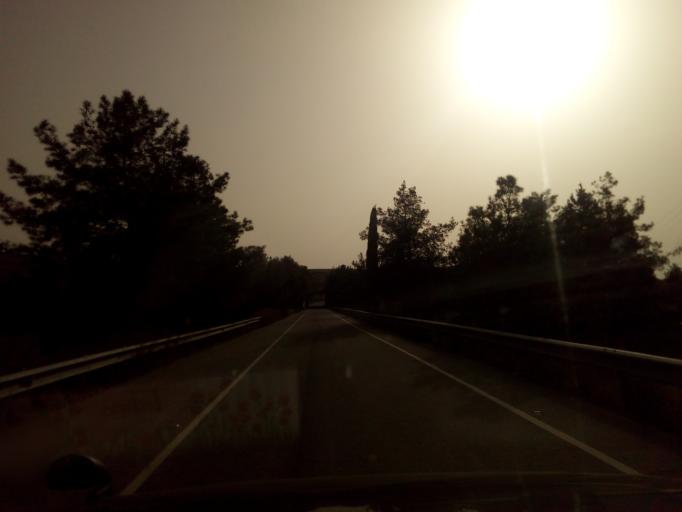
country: CY
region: Lefkosia
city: Lympia
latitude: 34.9954
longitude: 33.4863
